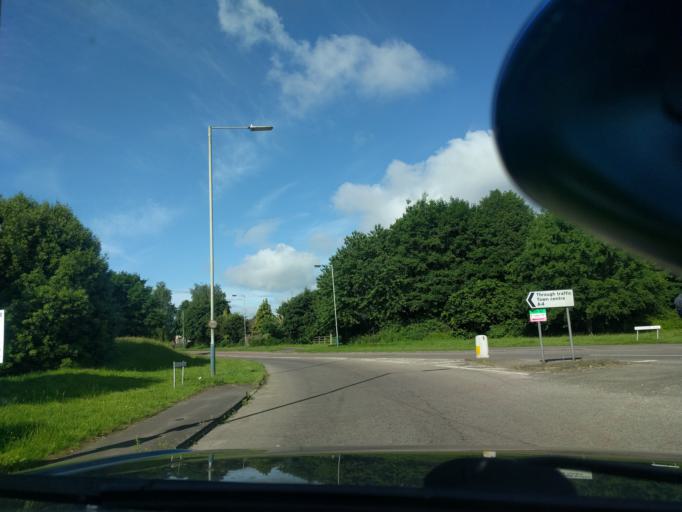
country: GB
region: England
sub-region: Wiltshire
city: Chippenham
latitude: 51.4483
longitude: -2.0917
